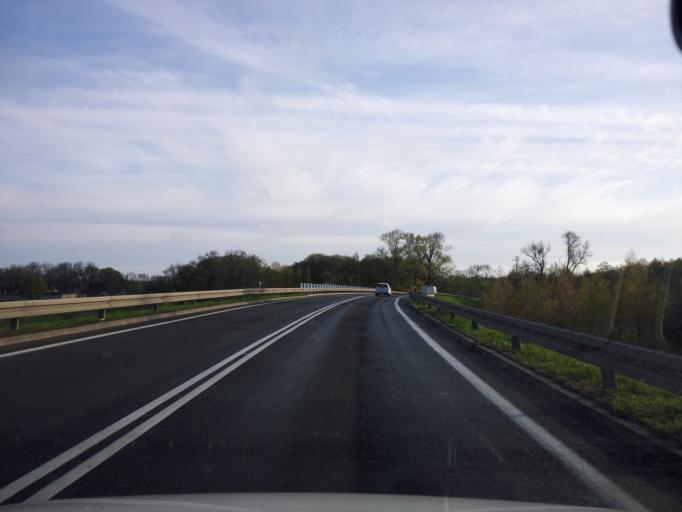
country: PL
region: Lubusz
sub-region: Powiat zarski
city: Zary
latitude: 51.6509
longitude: 15.1159
